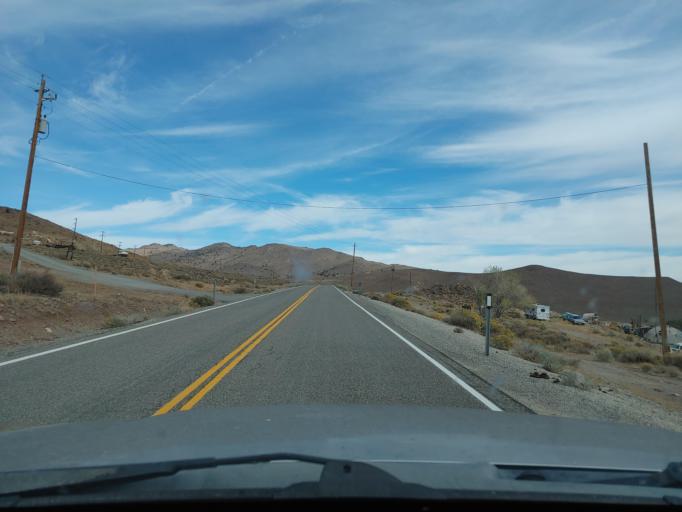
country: US
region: Nevada
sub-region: Lyon County
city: Dayton
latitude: 39.2344
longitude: -119.6432
